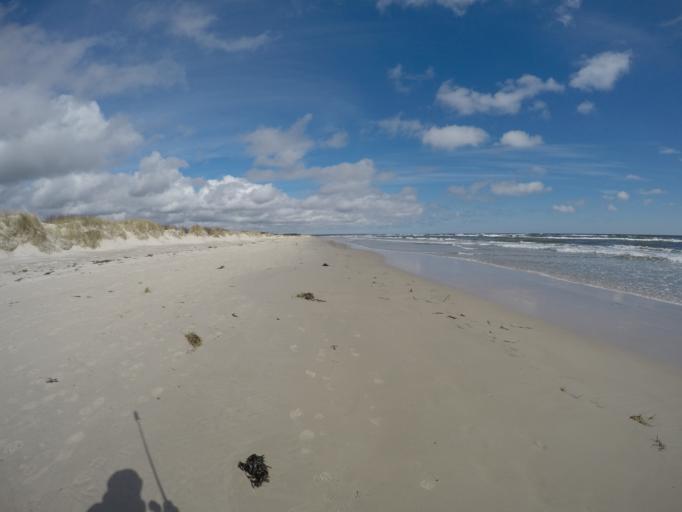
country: SE
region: Skane
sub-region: Simrishamns Kommun
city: Simrishamn
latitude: 55.3994
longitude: 14.2143
